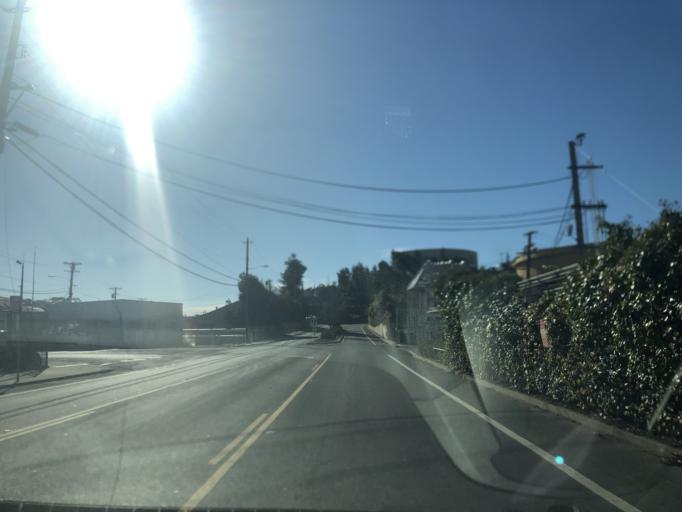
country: US
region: California
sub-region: Contra Costa County
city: Martinez
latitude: 38.0232
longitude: -122.1250
